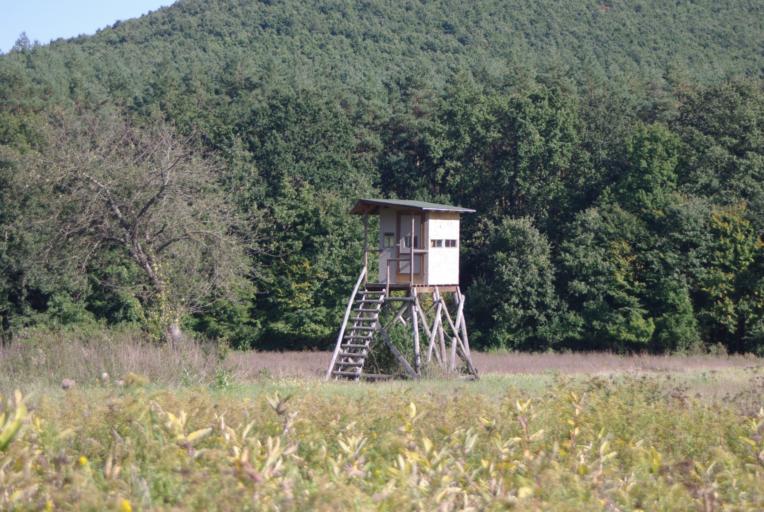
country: HU
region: Pest
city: Kosd
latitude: 47.8469
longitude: 19.1651
